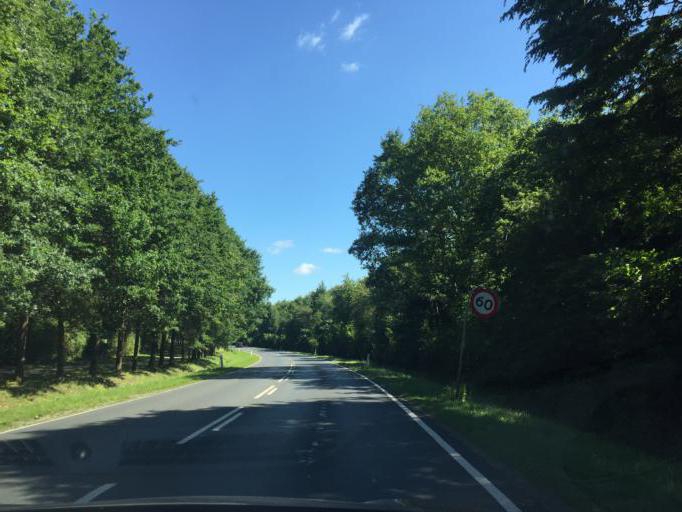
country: DK
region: South Denmark
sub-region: Odense Kommune
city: Bellinge
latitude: 55.3767
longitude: 10.3416
